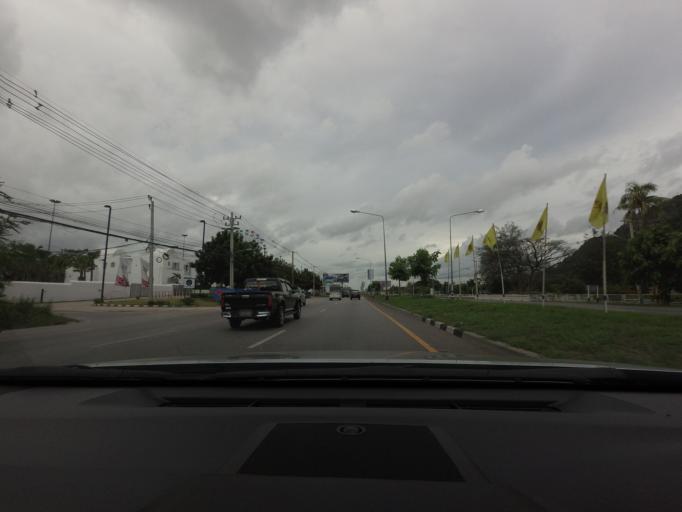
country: TH
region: Phetchaburi
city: Cha-am
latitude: 12.8303
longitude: 99.9349
